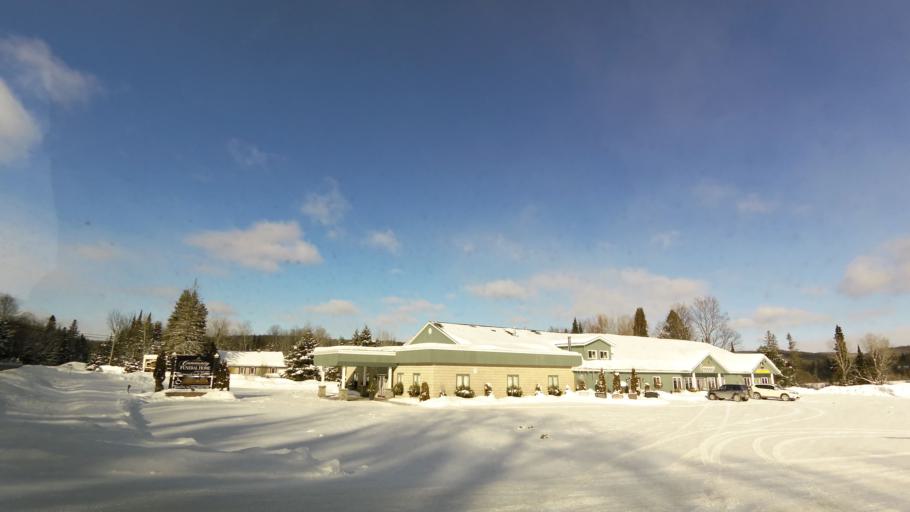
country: CA
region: Ontario
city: Bancroft
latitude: 45.0612
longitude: -78.5218
